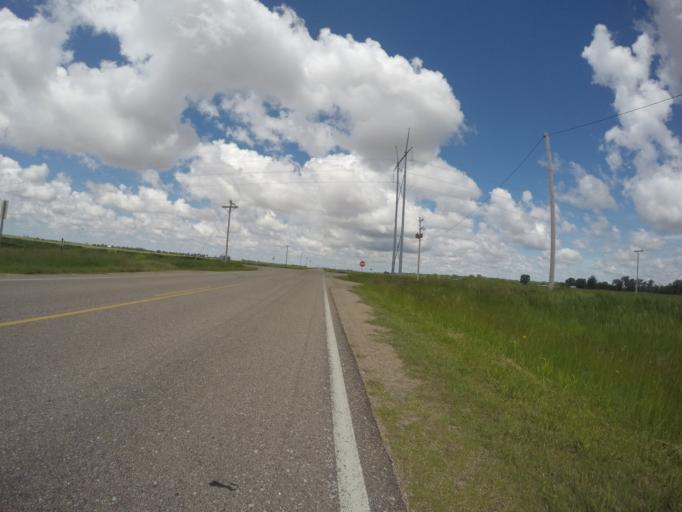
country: US
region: Nebraska
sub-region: Buffalo County
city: Kearney
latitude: 40.6570
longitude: -99.2557
